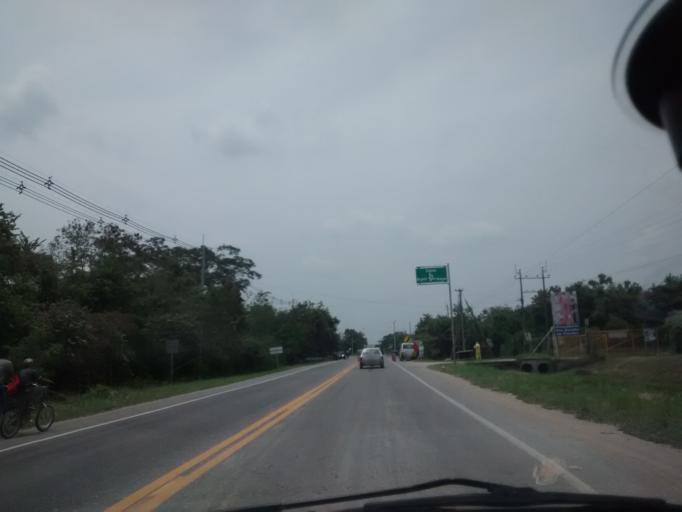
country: CO
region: Tolima
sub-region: Flandes
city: Flandes
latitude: 4.2597
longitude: -74.8262
